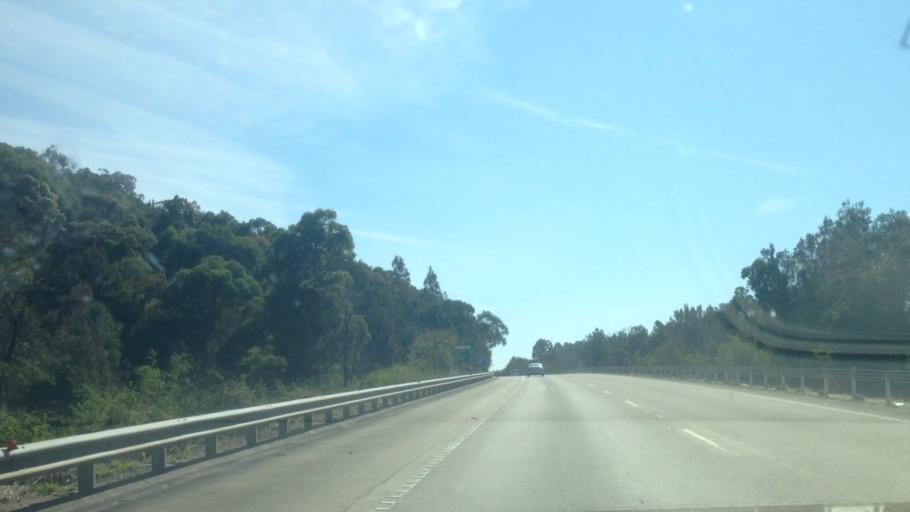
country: AU
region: New South Wales
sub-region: Lake Macquarie Shire
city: Fennell Bay
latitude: -32.9786
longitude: 151.5277
